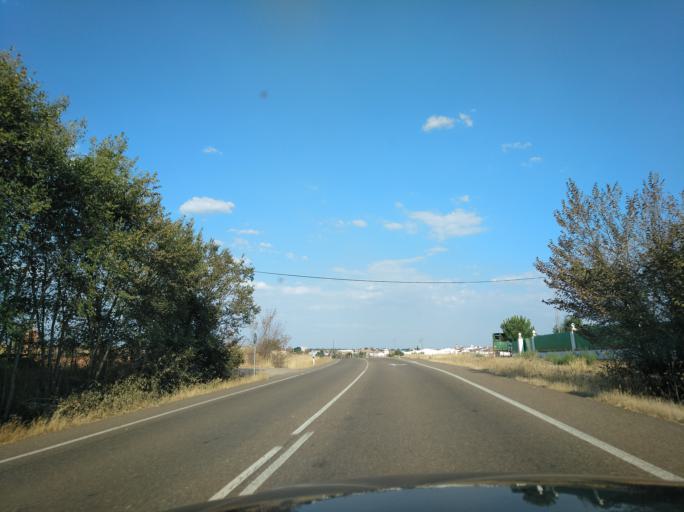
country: ES
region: Extremadura
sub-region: Provincia de Badajoz
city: Villanueva del Fresno
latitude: 38.3771
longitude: -7.1798
